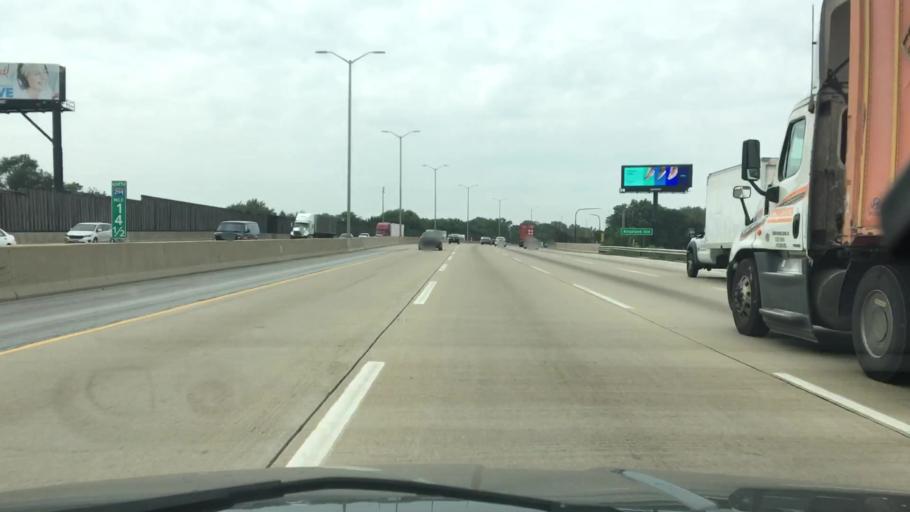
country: US
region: Illinois
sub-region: Cook County
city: Chicago Ridge
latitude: 41.6817
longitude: -87.7779
